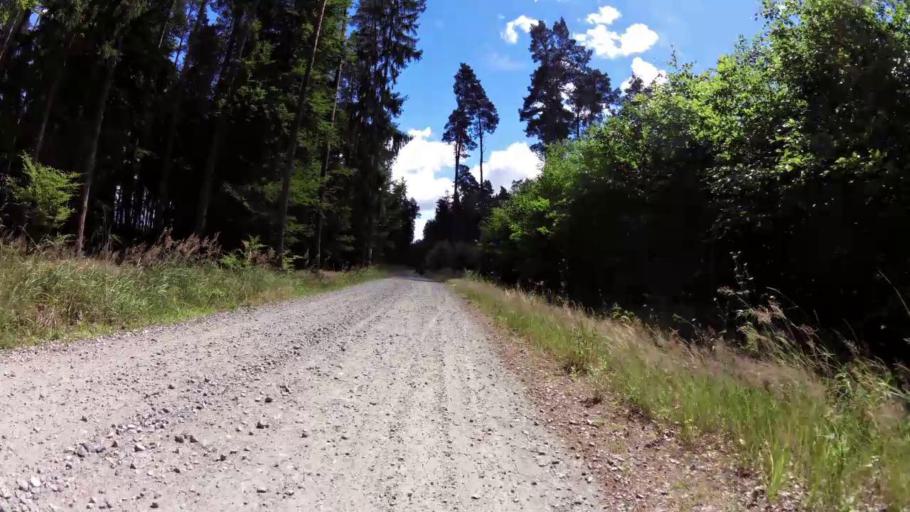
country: PL
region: West Pomeranian Voivodeship
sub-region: Powiat lobeski
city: Radowo Male
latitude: 53.7243
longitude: 15.5344
